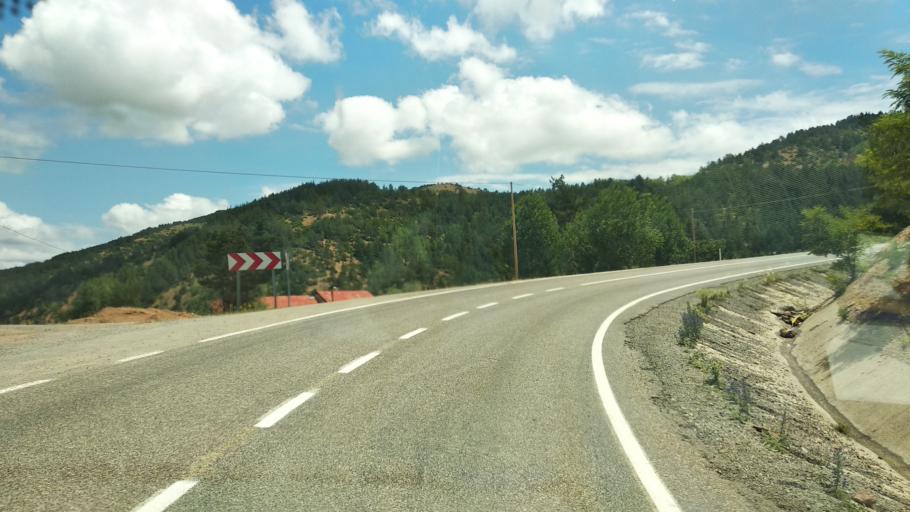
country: TR
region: Gumushane
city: Kose
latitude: 40.3010
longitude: 39.5561
